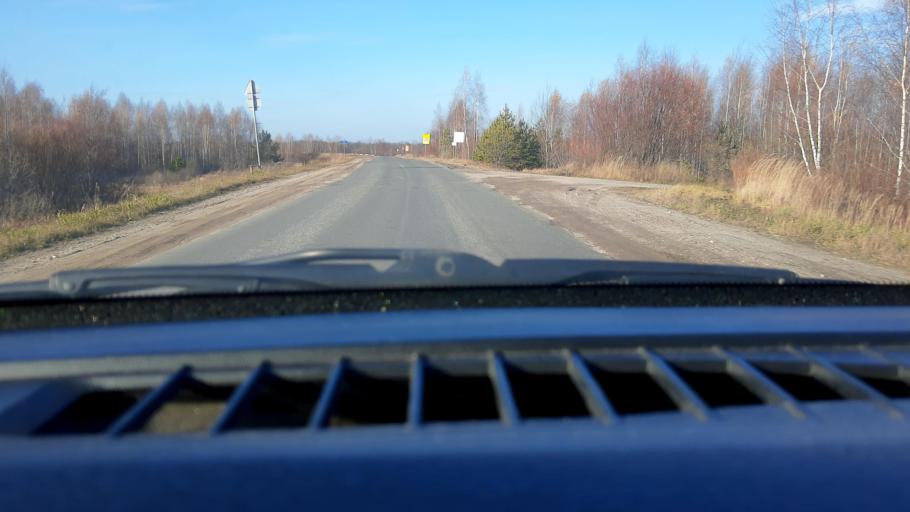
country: RU
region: Nizjnij Novgorod
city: Neklyudovo
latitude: 56.4213
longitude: 43.9317
